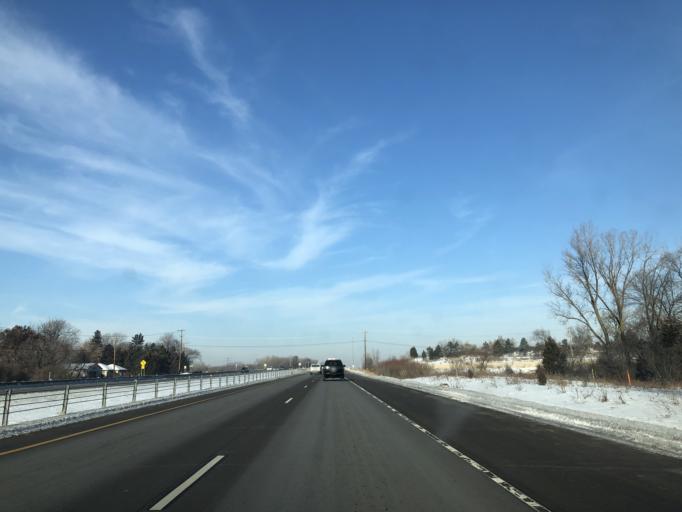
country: US
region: Minnesota
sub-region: Ramsey County
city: Shoreview
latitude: 45.0770
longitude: -93.1734
